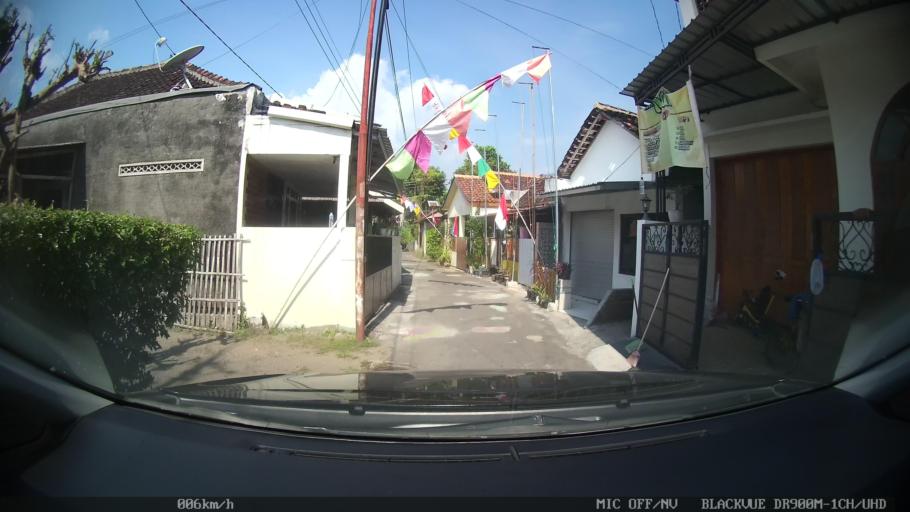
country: ID
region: Daerah Istimewa Yogyakarta
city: Yogyakarta
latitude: -7.8291
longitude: 110.3919
